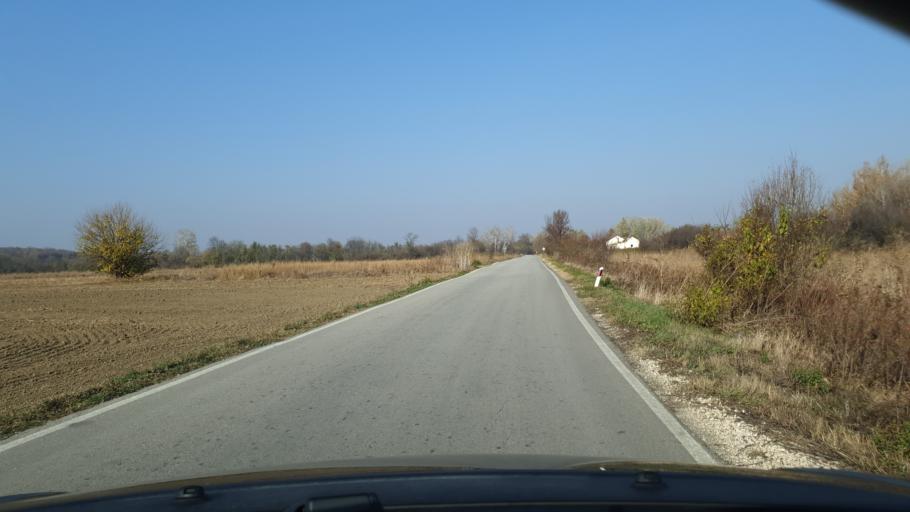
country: BG
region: Vidin
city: Bregovo
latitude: 44.1539
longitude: 22.6039
